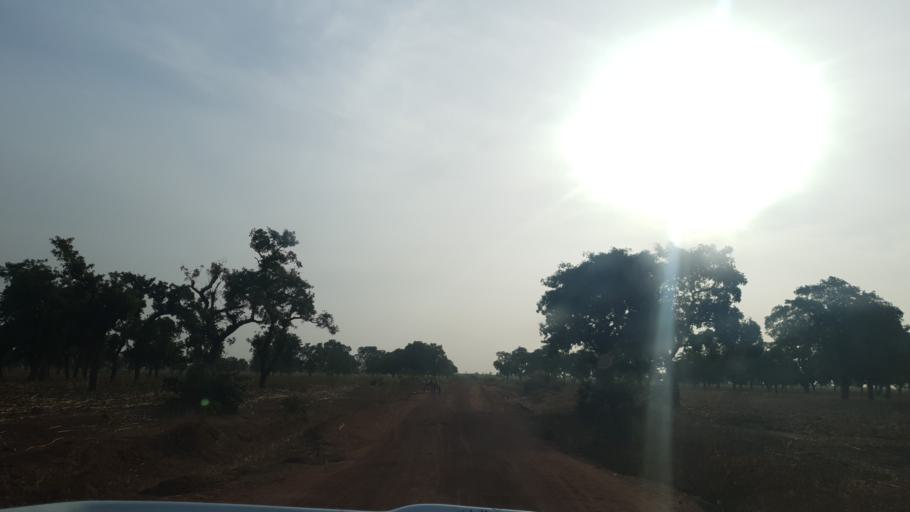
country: ML
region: Koulikoro
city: Dioila
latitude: 12.7701
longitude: -6.9293
